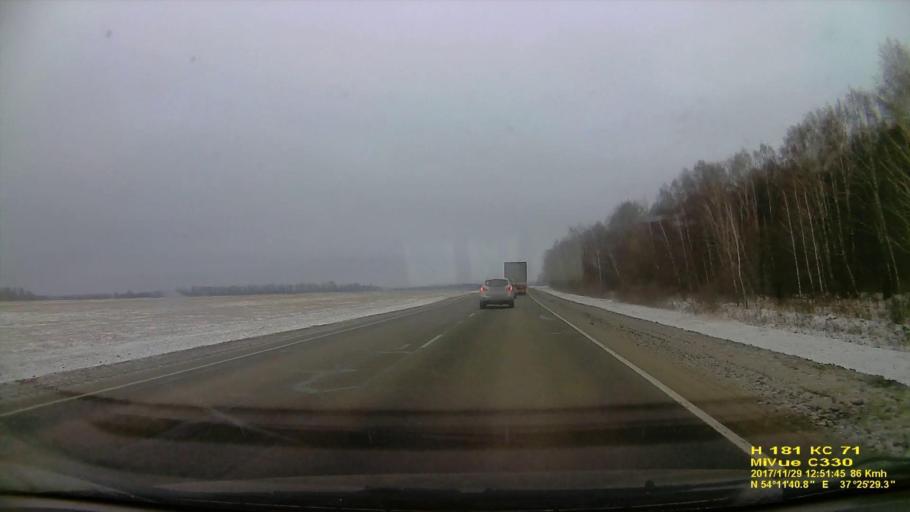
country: RU
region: Tula
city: Barsuki
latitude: 54.1947
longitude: 37.4248
